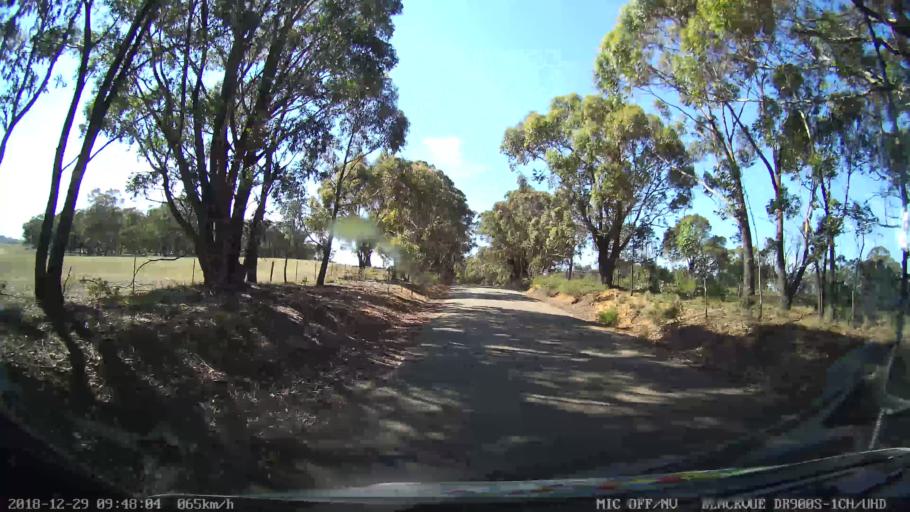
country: AU
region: New South Wales
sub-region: Upper Lachlan Shire
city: Crookwell
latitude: -34.7126
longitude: 149.4535
